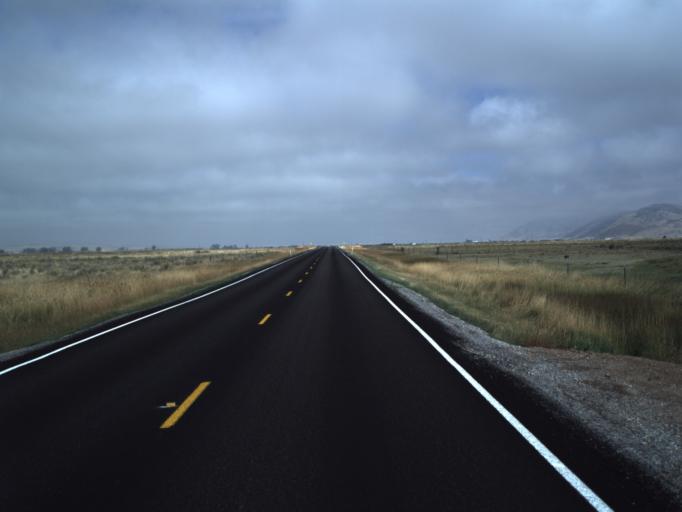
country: US
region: Utah
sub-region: Rich County
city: Randolph
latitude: 41.4914
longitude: -111.1195
